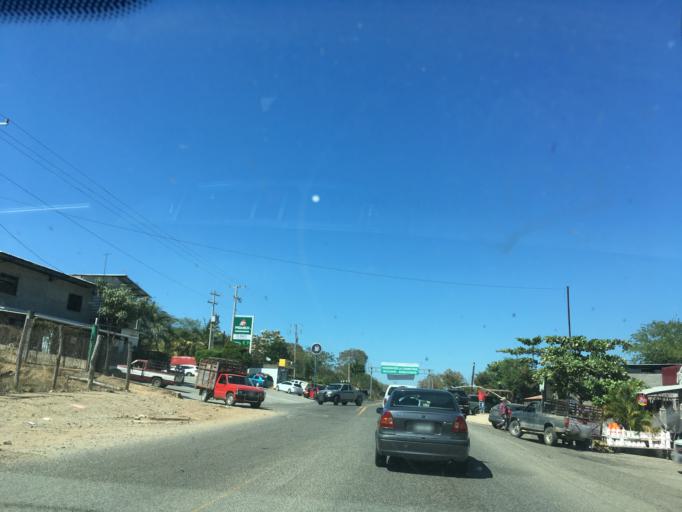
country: MX
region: Guerrero
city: La Union
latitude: 17.9370
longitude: -101.8300
